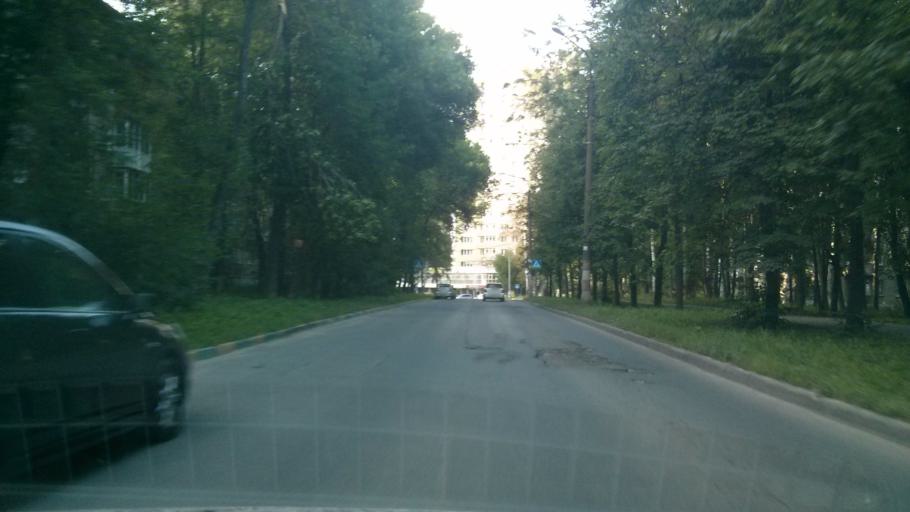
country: RU
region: Nizjnij Novgorod
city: Nizhniy Novgorod
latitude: 56.2922
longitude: 44.0438
